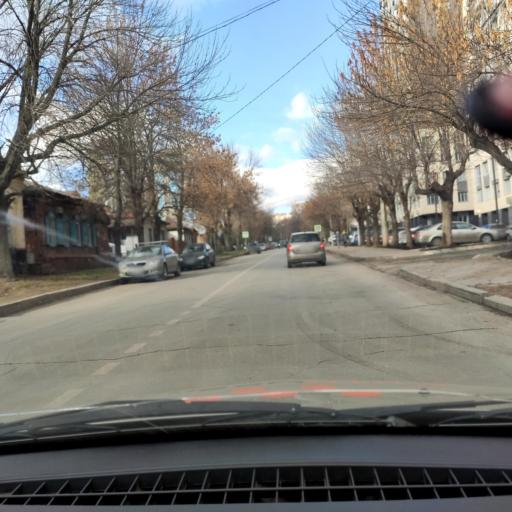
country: RU
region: Bashkortostan
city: Ufa
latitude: 54.7195
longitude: 55.9627
